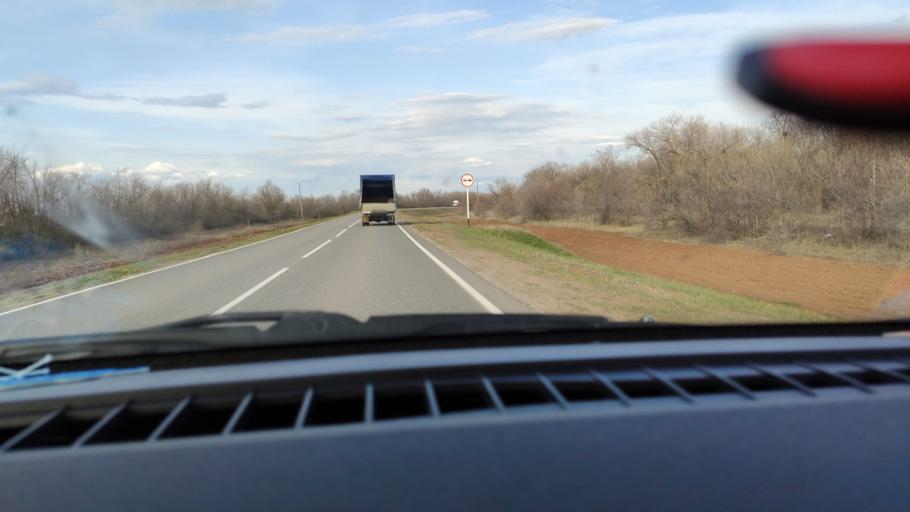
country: RU
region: Saratov
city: Privolzhskiy
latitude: 51.2898
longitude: 45.9809
